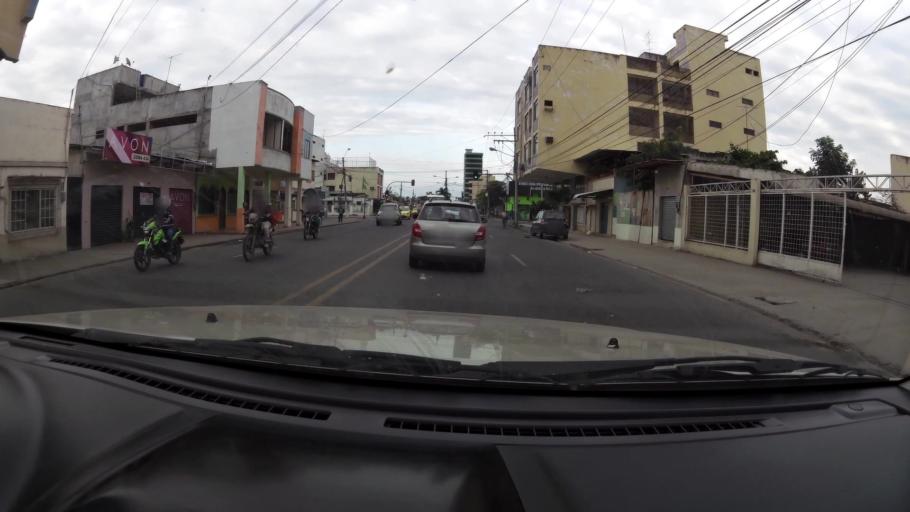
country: EC
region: El Oro
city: Machala
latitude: -3.2582
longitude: -79.9644
